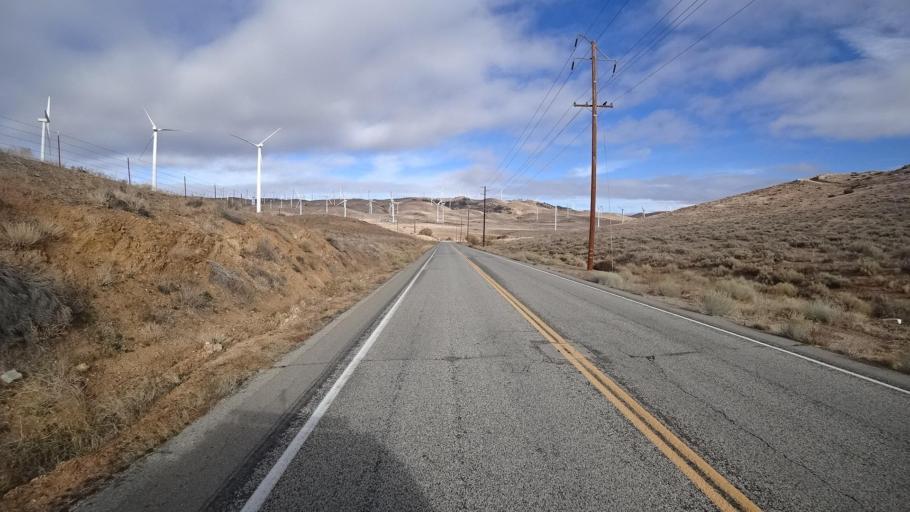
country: US
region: California
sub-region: Kern County
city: Tehachapi
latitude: 35.0448
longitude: -118.3534
